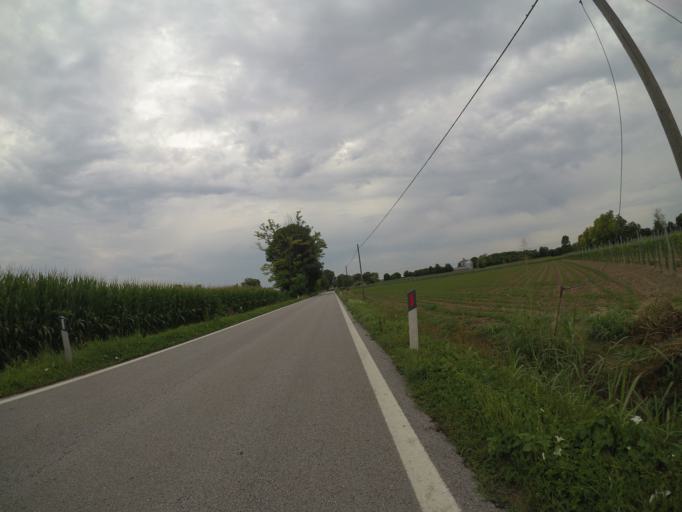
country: IT
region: Friuli Venezia Giulia
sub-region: Provincia di Udine
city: Camino al Tagliamento
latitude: 45.9007
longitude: 12.9447
